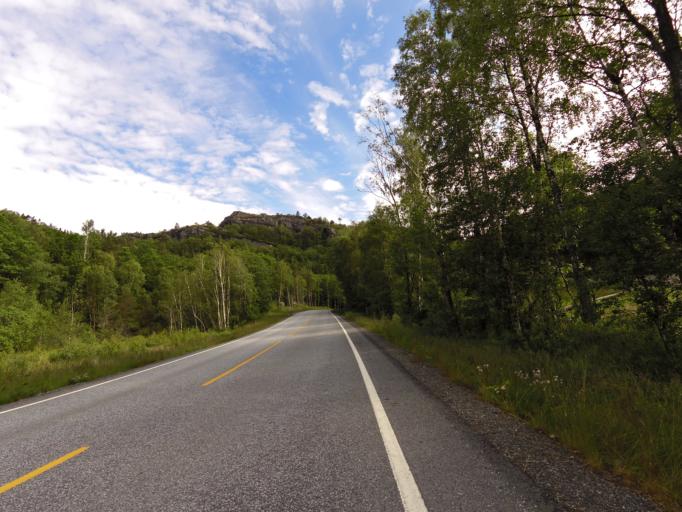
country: NO
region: Vest-Agder
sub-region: Lyngdal
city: Lyngdal
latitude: 58.0478
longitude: 7.1682
